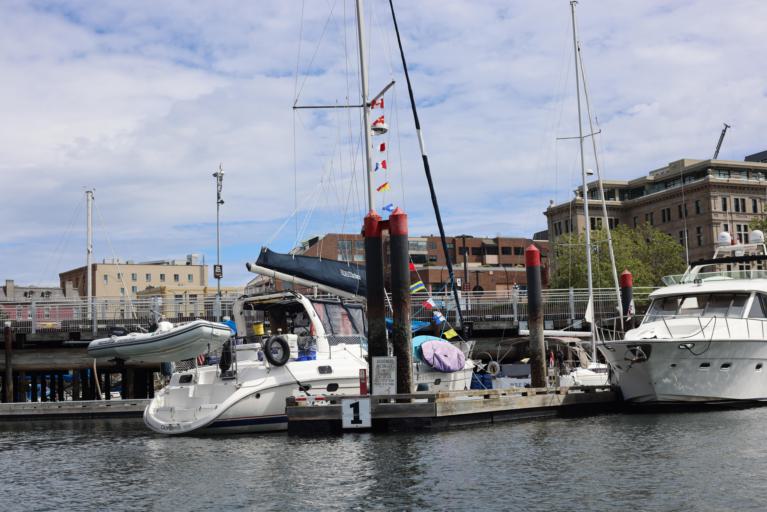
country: CA
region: British Columbia
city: Victoria
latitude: 48.4224
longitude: -123.3708
